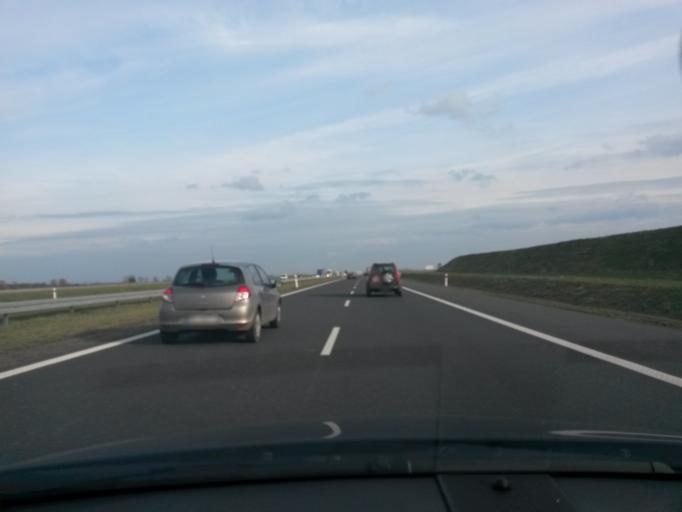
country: PL
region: Lodz Voivodeship
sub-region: Powiat poddebicki
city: Wartkowice
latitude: 51.9857
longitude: 19.0631
